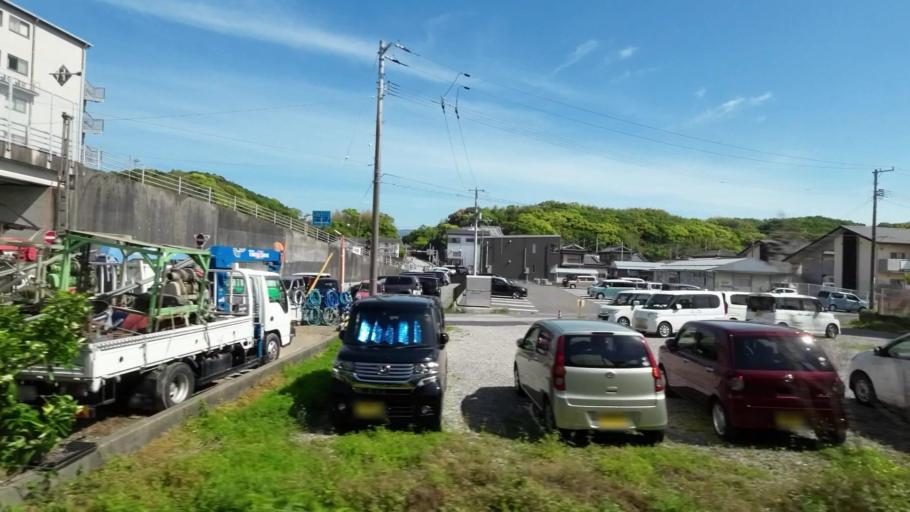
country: JP
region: Kochi
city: Kochi-shi
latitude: 33.5782
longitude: 133.6386
